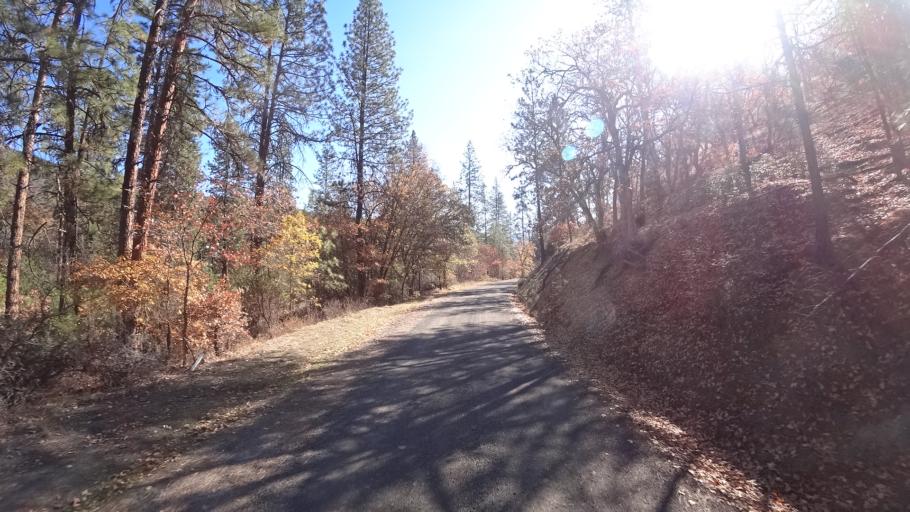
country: US
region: California
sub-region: Siskiyou County
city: Yreka
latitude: 41.8631
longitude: -122.7084
